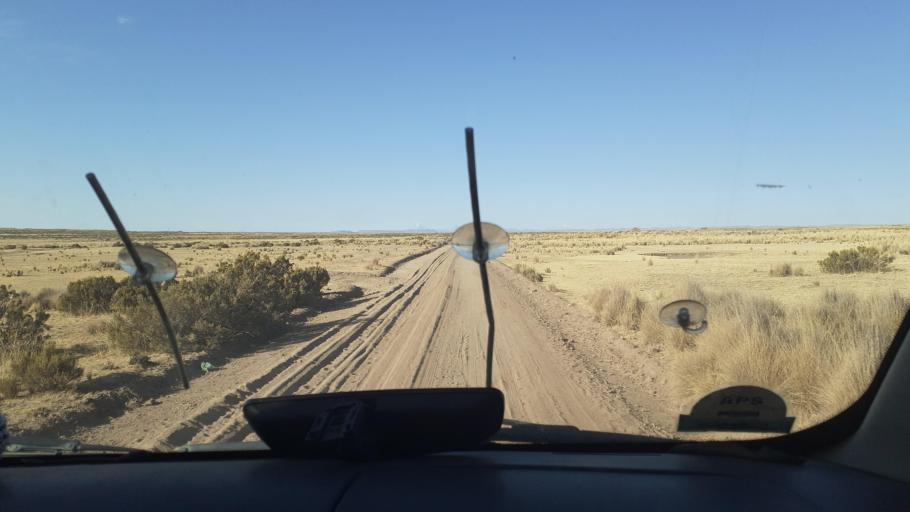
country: BO
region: La Paz
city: Tiahuanaco
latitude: -17.0434
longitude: -68.7559
